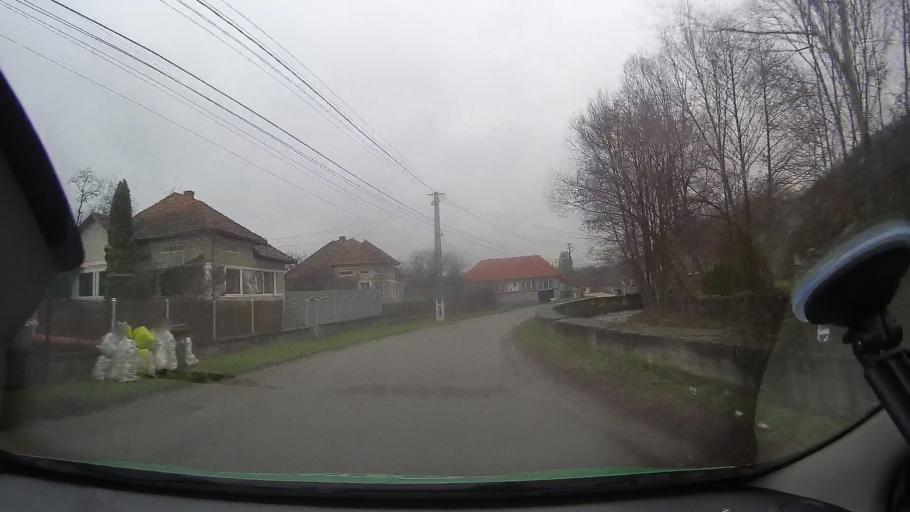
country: RO
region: Arad
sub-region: Comuna Halmagel
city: Halmagel
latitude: 46.2688
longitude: 22.6200
